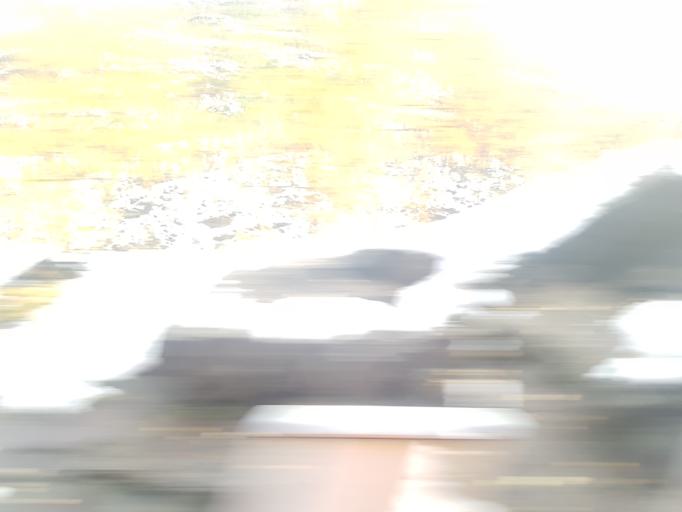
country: NO
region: Sor-Trondelag
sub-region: Oppdal
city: Oppdal
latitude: 62.3908
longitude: 9.6369
